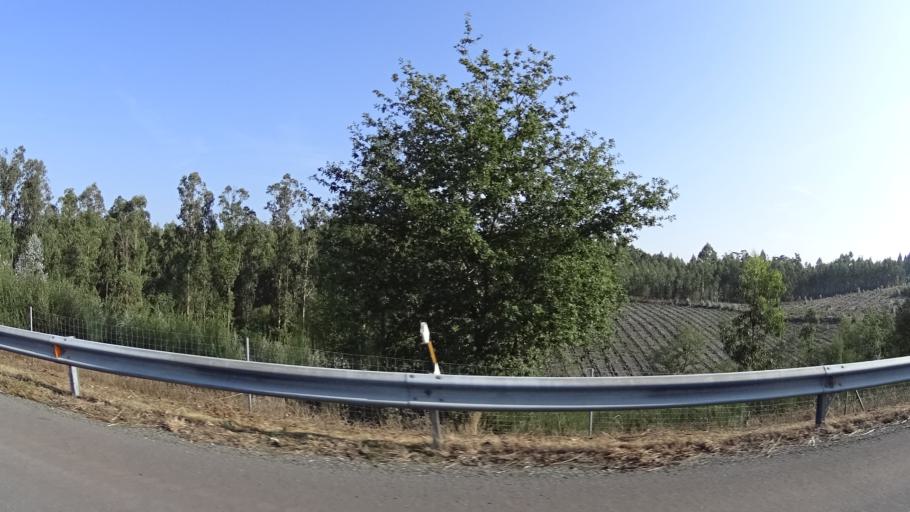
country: ES
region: Galicia
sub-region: Provincia da Coruna
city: Coiros
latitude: 43.2451
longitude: -8.1475
